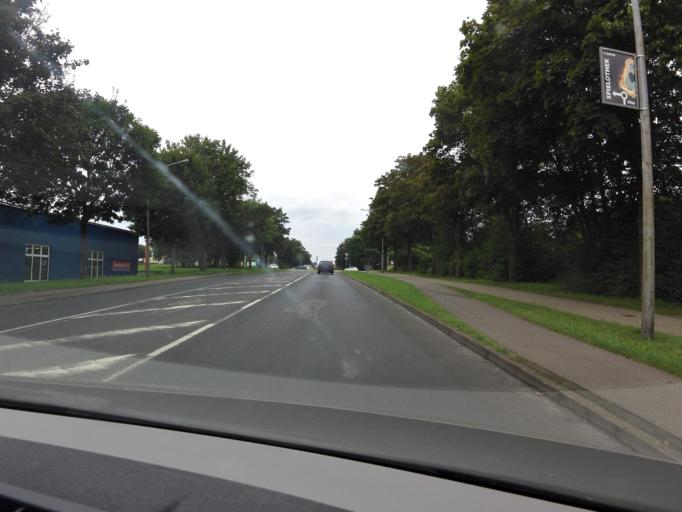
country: DE
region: Mecklenburg-Vorpommern
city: Neustrelitz
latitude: 53.3502
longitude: 13.0787
